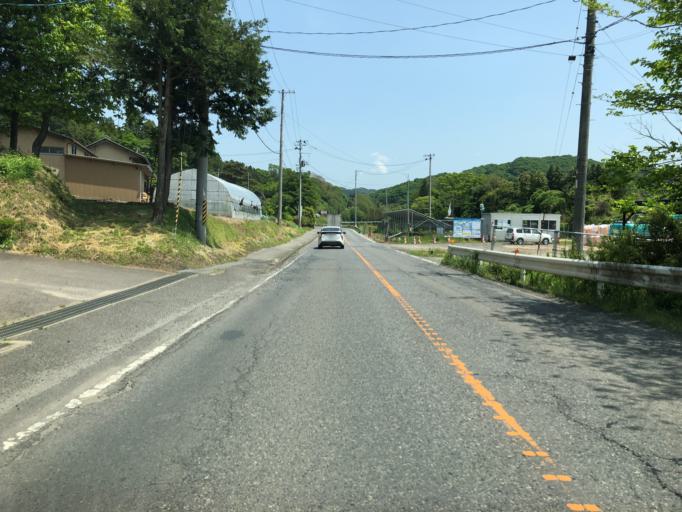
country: JP
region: Fukushima
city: Ishikawa
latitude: 37.1398
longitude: 140.4226
